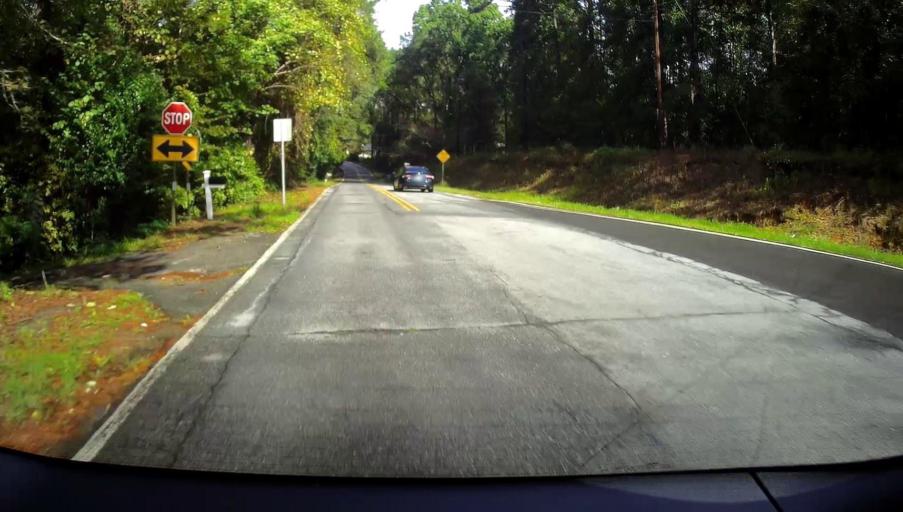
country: US
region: Georgia
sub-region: Bibb County
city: Macon
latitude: 32.9115
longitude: -83.7165
